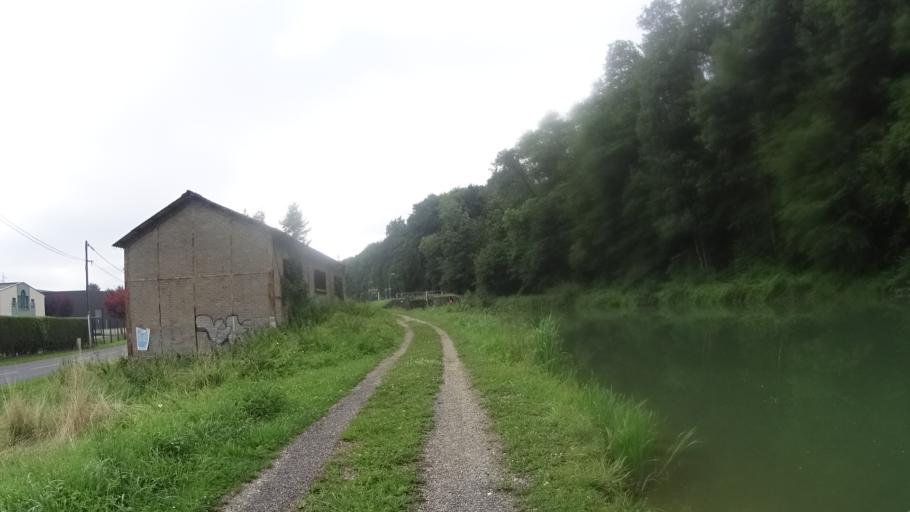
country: FR
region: Lorraine
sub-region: Departement de la Meuse
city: Fains-Veel
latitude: 48.8045
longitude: 5.1033
